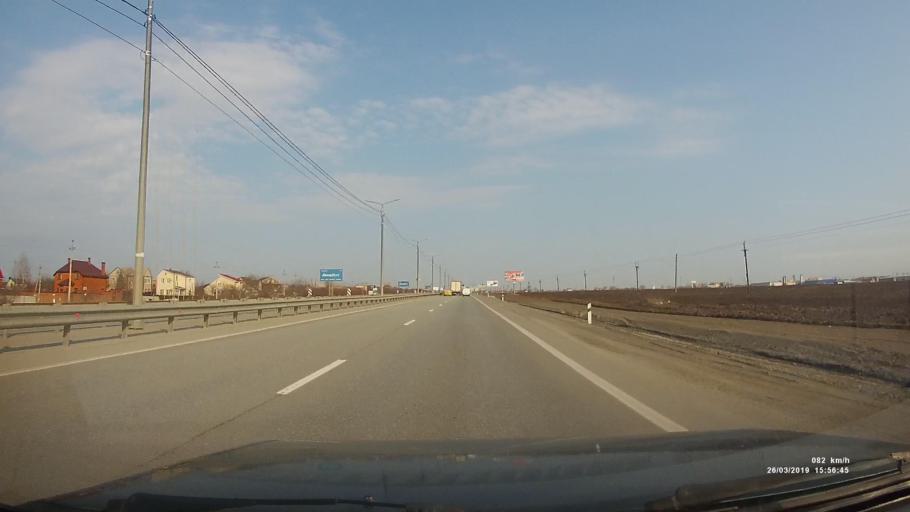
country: RU
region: Rostov
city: Kalinin
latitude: 47.2643
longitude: 39.5991
